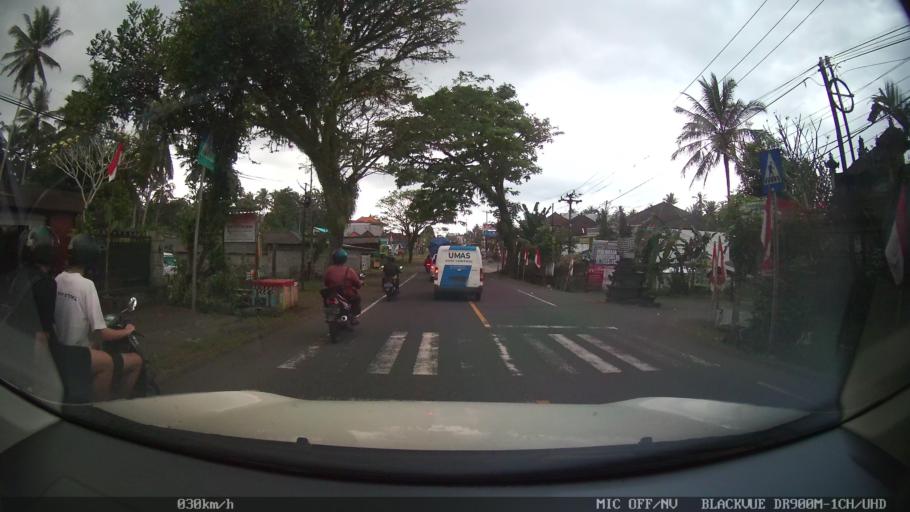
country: ID
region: Bali
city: Banjar Bantasbaleagung
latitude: -8.5016
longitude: 115.0625
